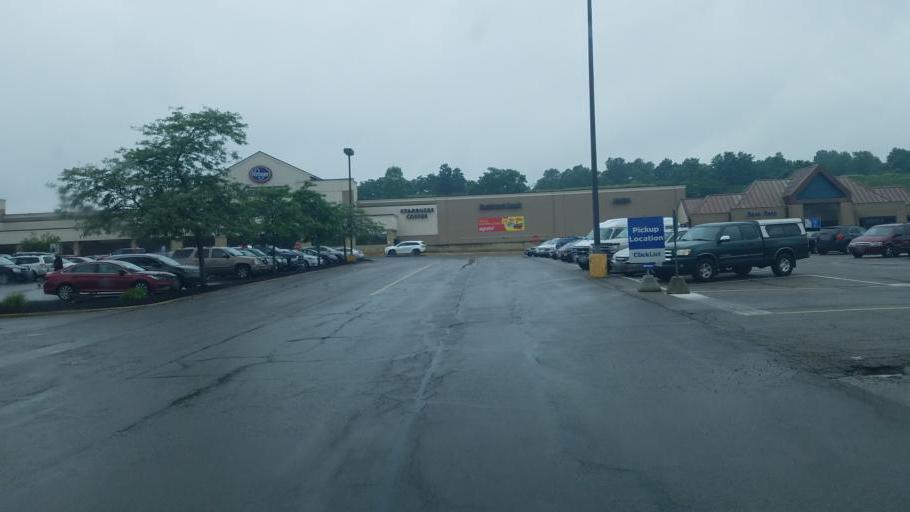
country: US
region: Ohio
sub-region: Richland County
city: Mansfield
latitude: 40.7184
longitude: -82.5480
